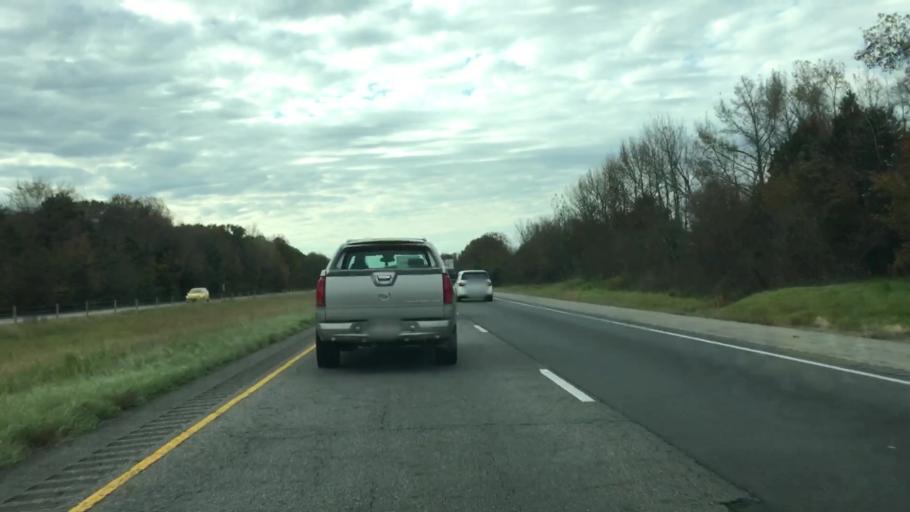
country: US
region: Arkansas
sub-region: Conway County
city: Morrilton
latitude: 35.1625
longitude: -92.6130
